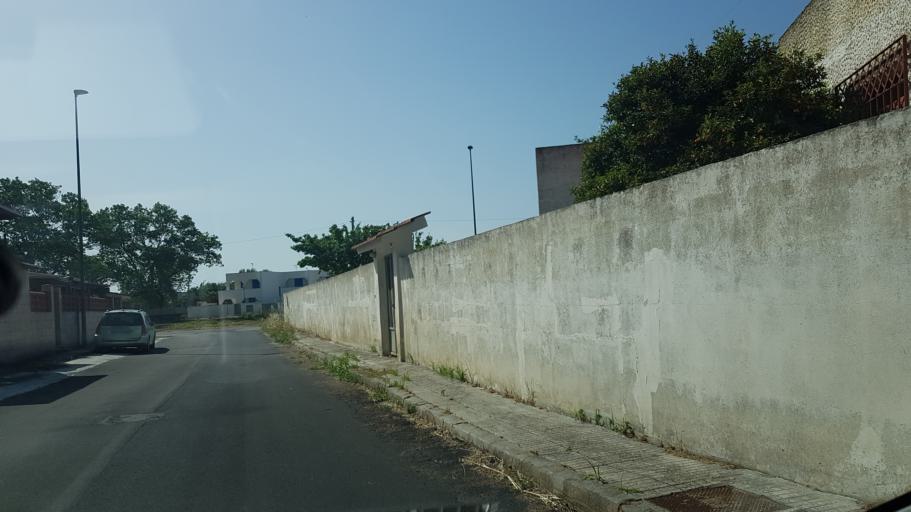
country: IT
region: Apulia
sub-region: Provincia di Brindisi
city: Torchiarolo
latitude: 40.5148
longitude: 18.0886
